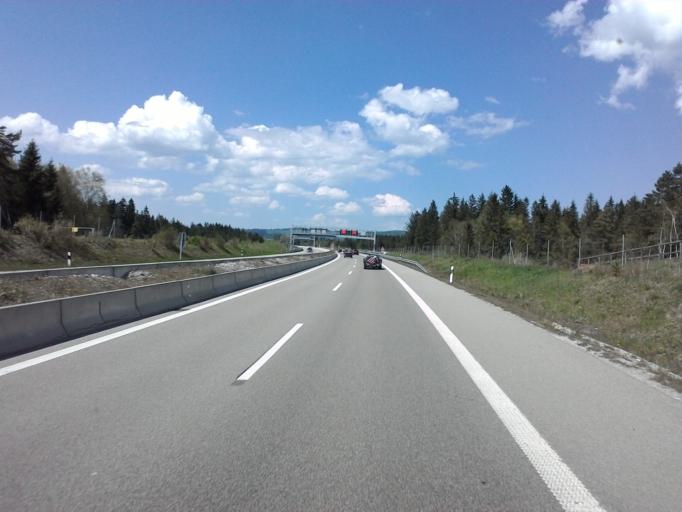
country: DE
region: Bavaria
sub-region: Swabia
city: Fuessen
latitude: 47.5802
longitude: 10.6623
